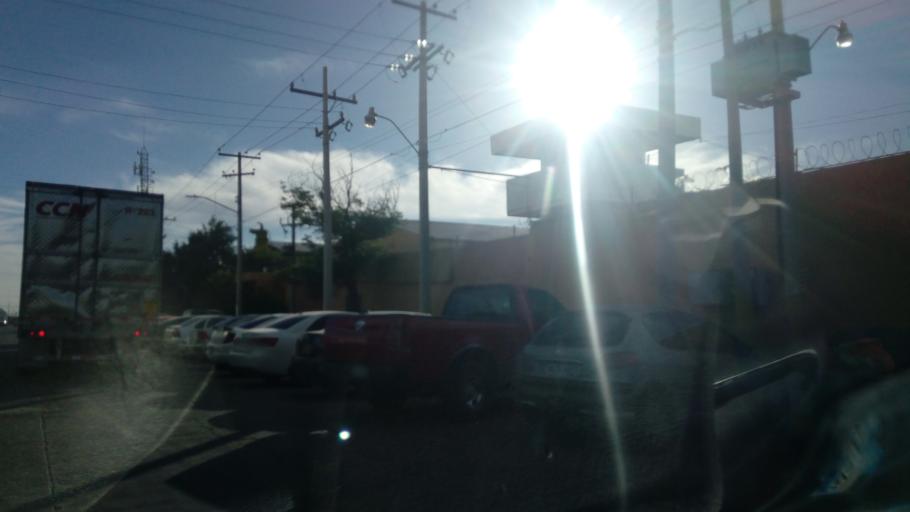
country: MX
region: Durango
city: Victoria de Durango
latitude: 24.0689
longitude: -104.6067
